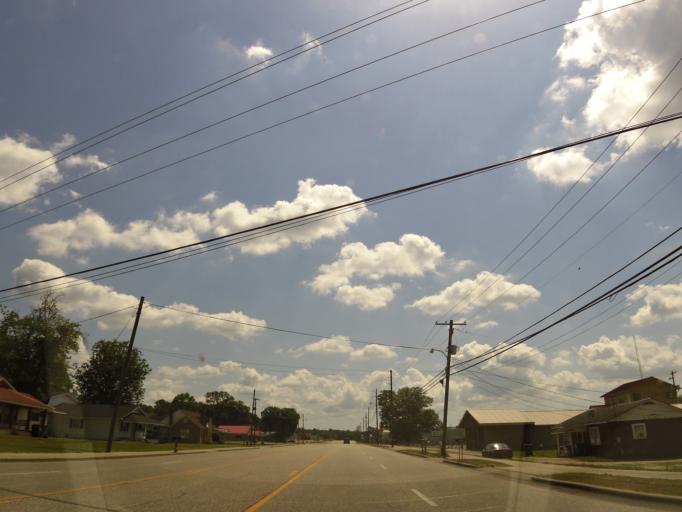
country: US
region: Alabama
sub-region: Marion County
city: Guin
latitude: 33.9663
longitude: -87.9042
